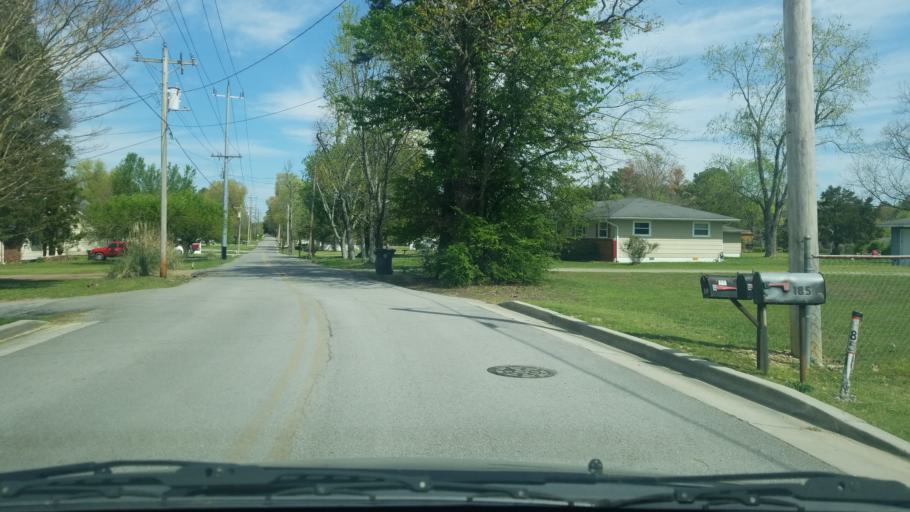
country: US
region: Georgia
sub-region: Catoosa County
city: Fort Oglethorpe
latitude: 34.9570
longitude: -85.2468
